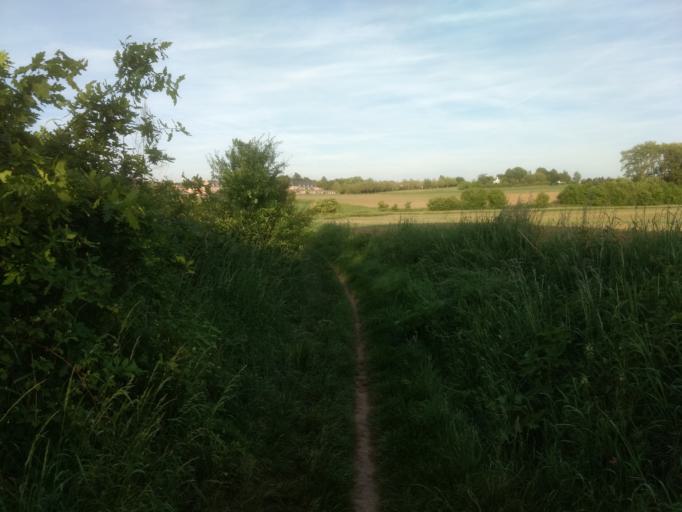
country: BE
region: Flanders
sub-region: Provincie Vlaams-Brabant
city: Bierbeek
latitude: 50.8526
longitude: 4.7412
